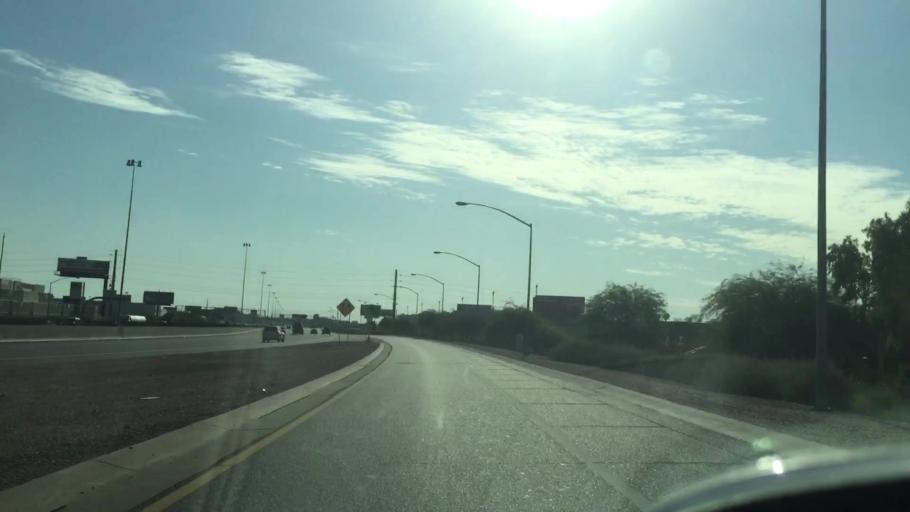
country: US
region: Arizona
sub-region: Maricopa County
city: Guadalupe
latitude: 33.4107
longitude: -112.0076
